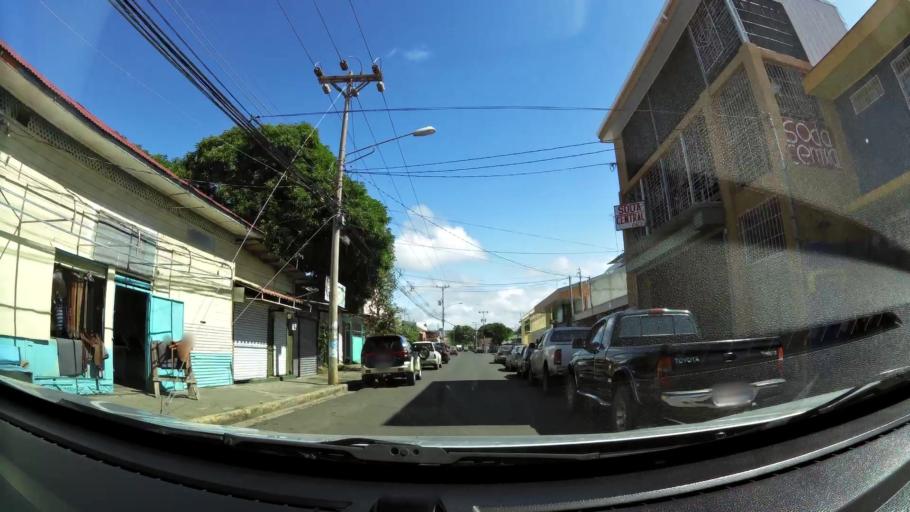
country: CR
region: Guanacaste
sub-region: Canton de Canas
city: Canas
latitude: 10.4268
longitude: -85.0897
